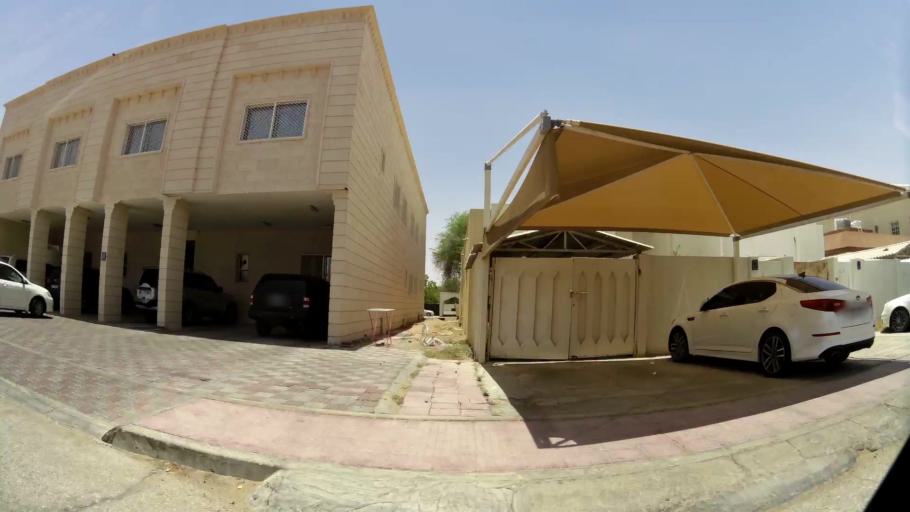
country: OM
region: Al Buraimi
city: Al Buraymi
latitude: 24.2598
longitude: 55.7325
